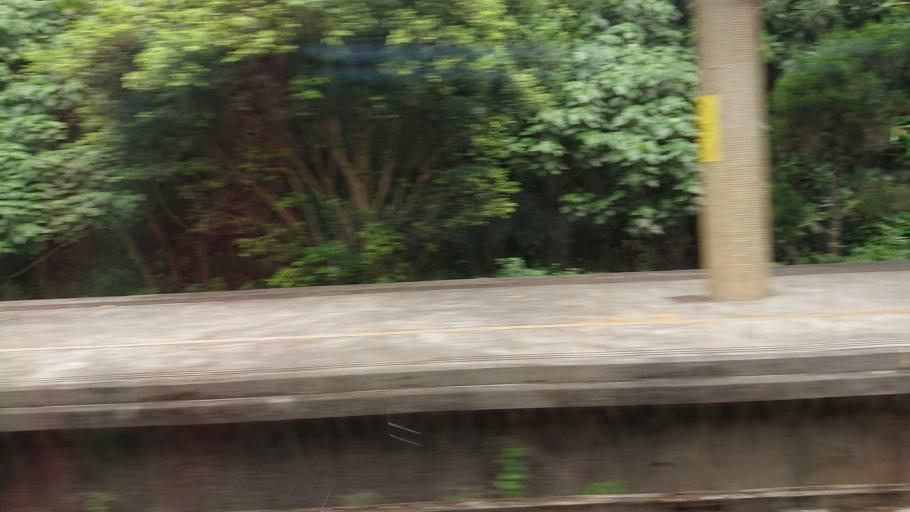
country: TW
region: Taiwan
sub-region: Yilan
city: Yilan
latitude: 24.9383
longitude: 121.8896
